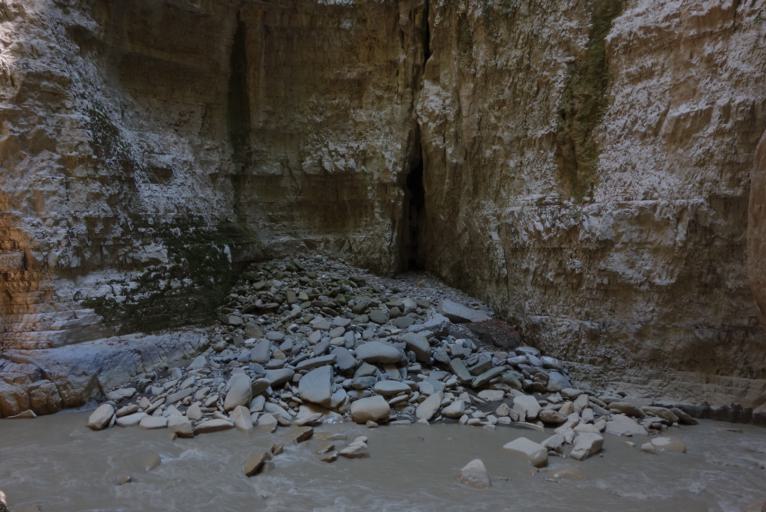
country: AL
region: Gjirokaster
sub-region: Rrethi i Permetit
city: Petran
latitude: 40.2573
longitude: 20.4614
